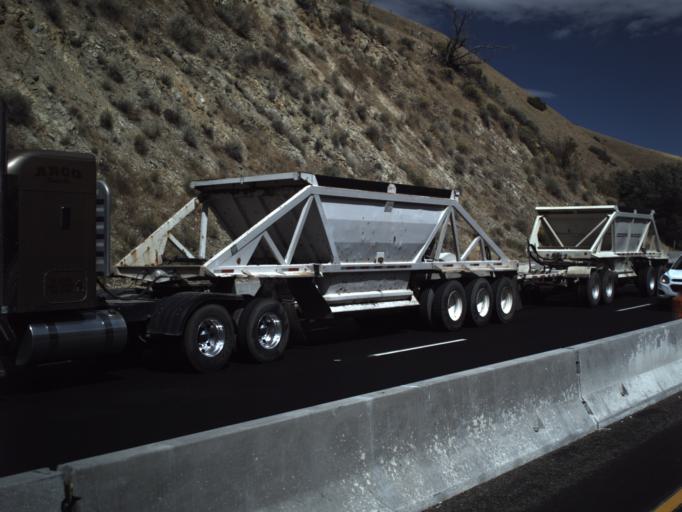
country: US
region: Utah
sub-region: Box Elder County
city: Brigham City
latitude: 41.4963
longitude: -111.9590
